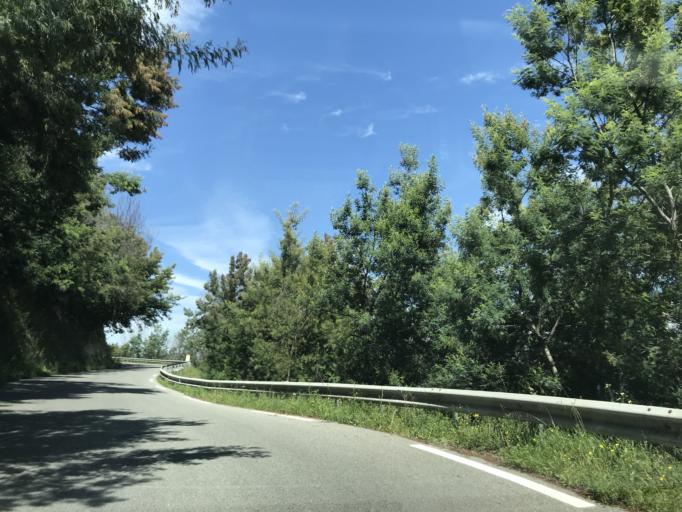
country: FR
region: Provence-Alpes-Cote d'Azur
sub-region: Departement du Var
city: Tanneron
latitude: 43.5870
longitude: 6.8848
